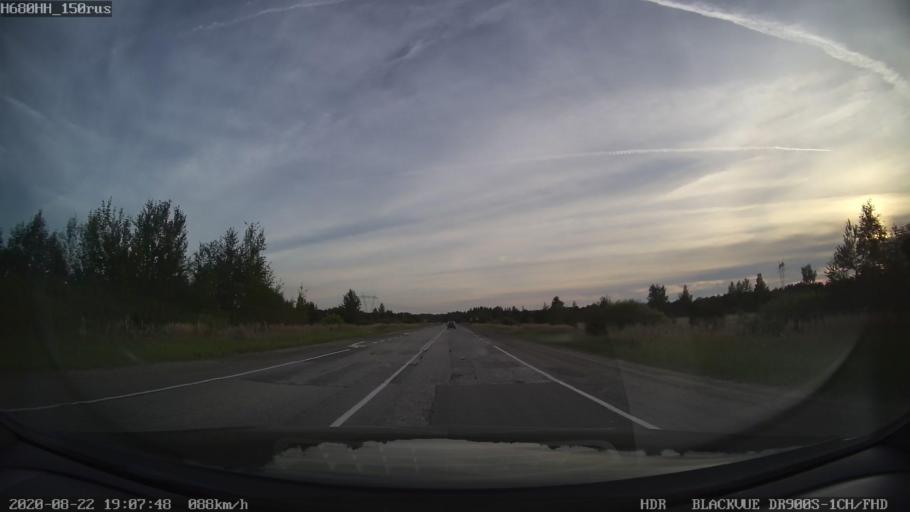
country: RU
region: Tverskaya
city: Sakharovo
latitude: 57.0527
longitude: 36.0873
